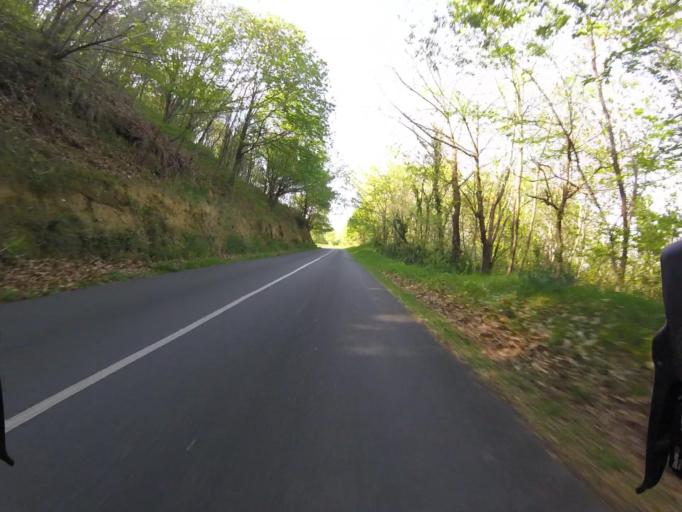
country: ES
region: Basque Country
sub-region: Provincia de Guipuzcoa
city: Fuenterrabia
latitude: 43.3684
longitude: -1.8272
